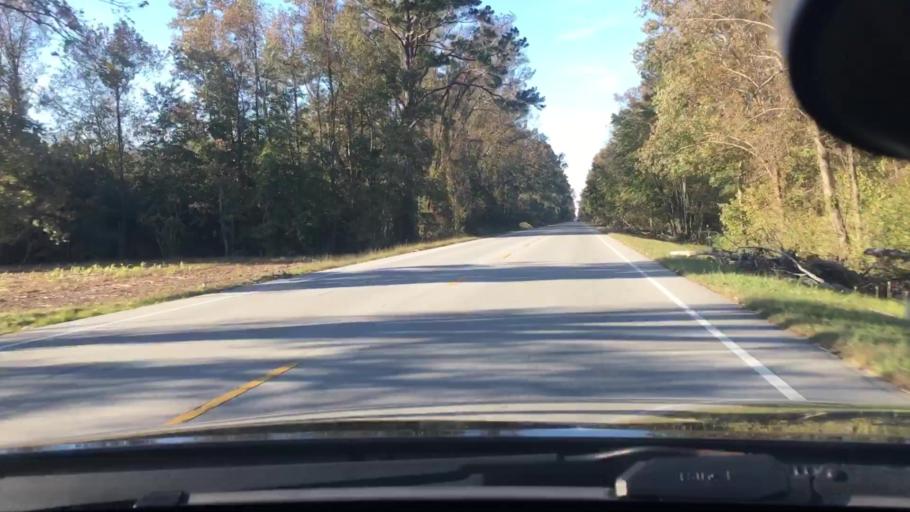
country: US
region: North Carolina
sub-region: Craven County
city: New Bern
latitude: 35.1819
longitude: -77.0482
